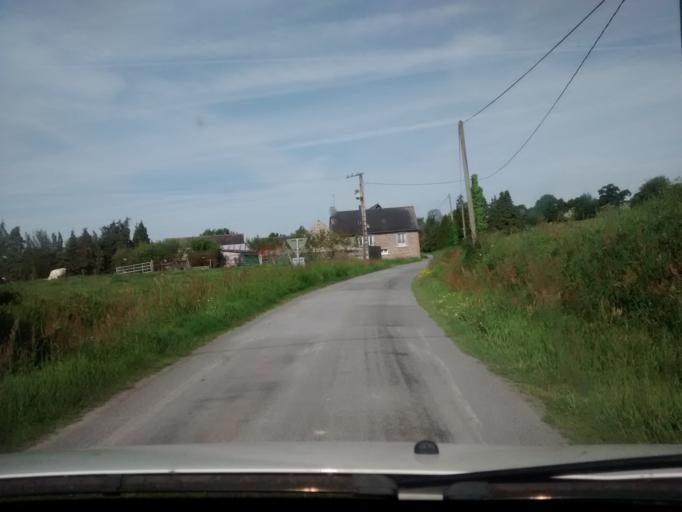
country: FR
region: Brittany
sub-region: Departement d'Ille-et-Vilaine
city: Javene
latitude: 48.3326
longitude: -1.2168
